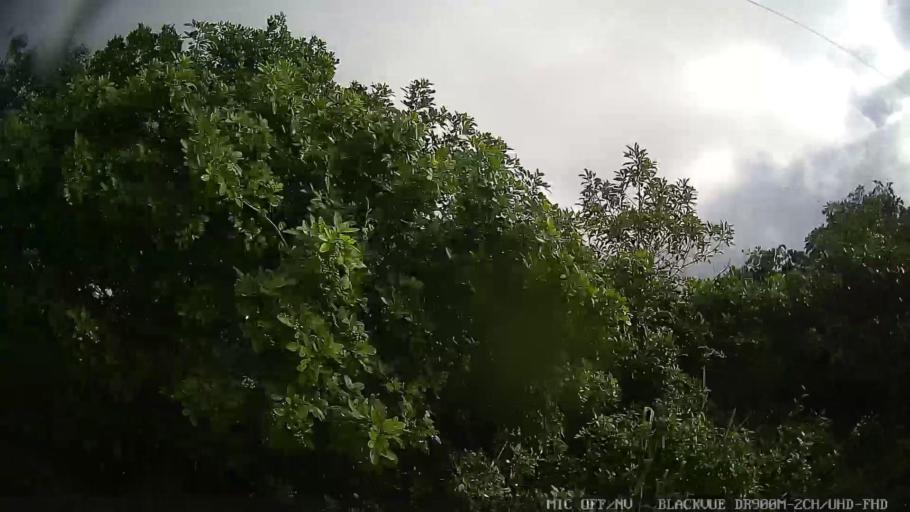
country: BR
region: Sao Paulo
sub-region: Peruibe
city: Peruibe
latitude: -24.2465
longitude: -46.9000
